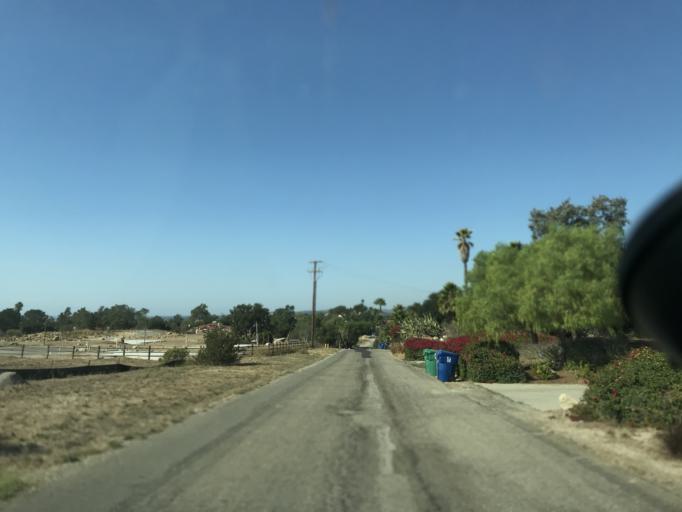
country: US
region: California
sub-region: Santa Barbara County
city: Goleta
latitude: 34.4588
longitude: -119.7841
